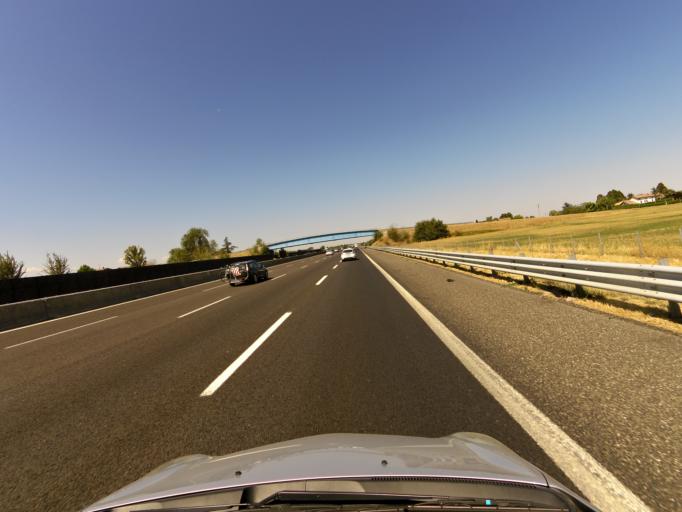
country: IT
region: Emilia-Romagna
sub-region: Provincia di Modena
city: San Cesario sul Panaro
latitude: 44.5681
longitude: 11.0295
